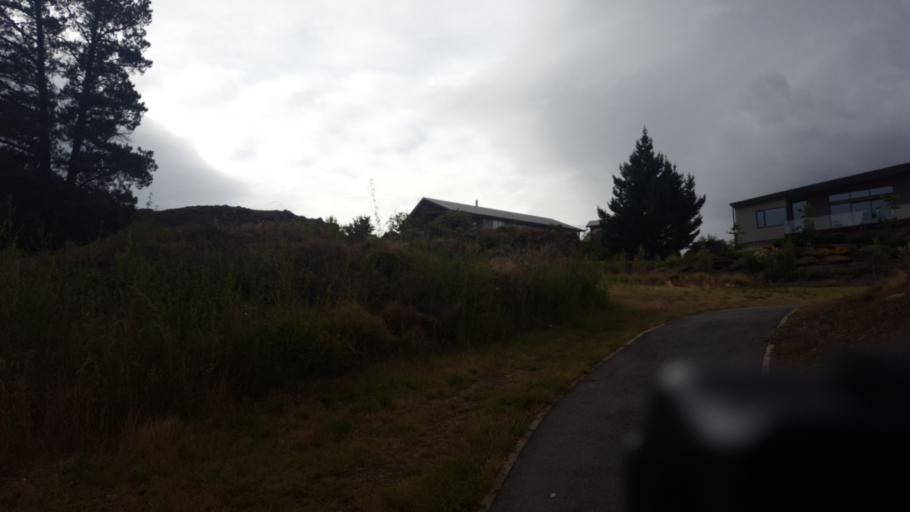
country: NZ
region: Otago
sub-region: Queenstown-Lakes District
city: Wanaka
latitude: -45.2509
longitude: 169.4040
